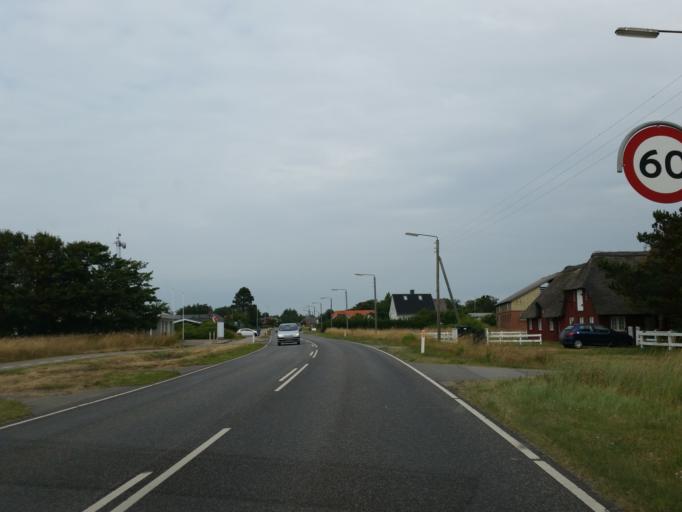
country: DE
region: Schleswig-Holstein
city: List
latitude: 55.1283
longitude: 8.5504
